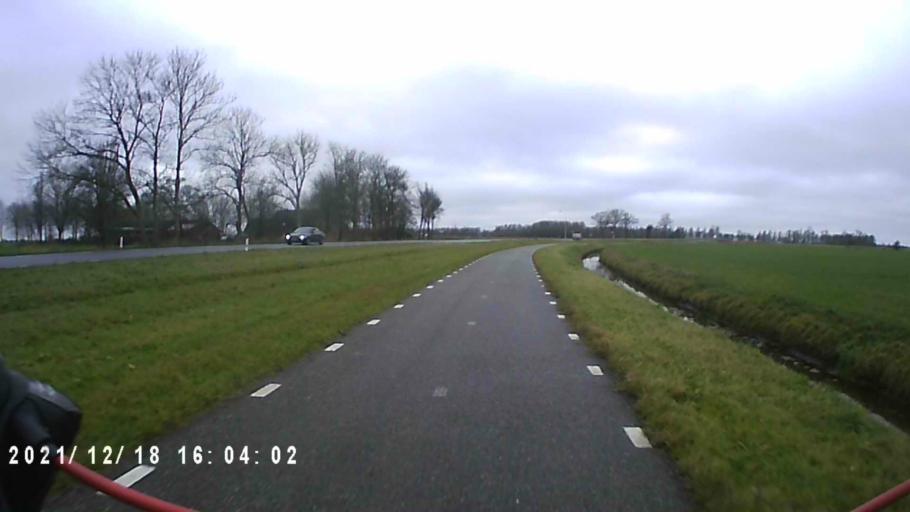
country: NL
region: Friesland
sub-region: Gemeente Dongeradeel
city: Anjum
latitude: 53.3510
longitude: 6.0789
